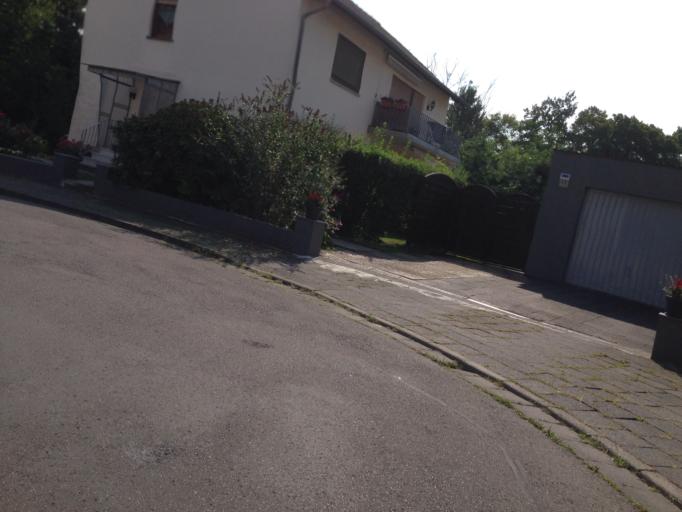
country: DE
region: Hesse
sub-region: Regierungsbezirk Giessen
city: Giessen
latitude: 50.5931
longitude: 8.7079
